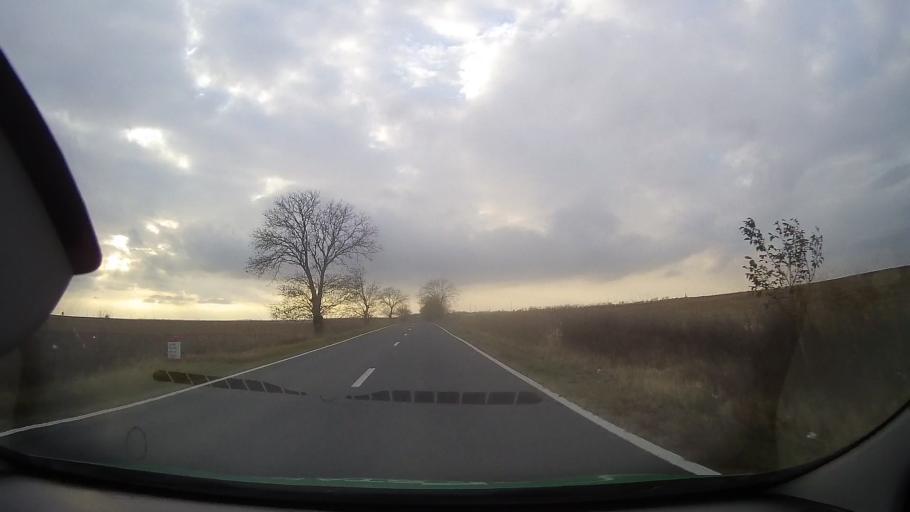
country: RO
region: Constanta
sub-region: Comuna Deleni
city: Deleni
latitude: 44.0887
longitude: 27.9884
